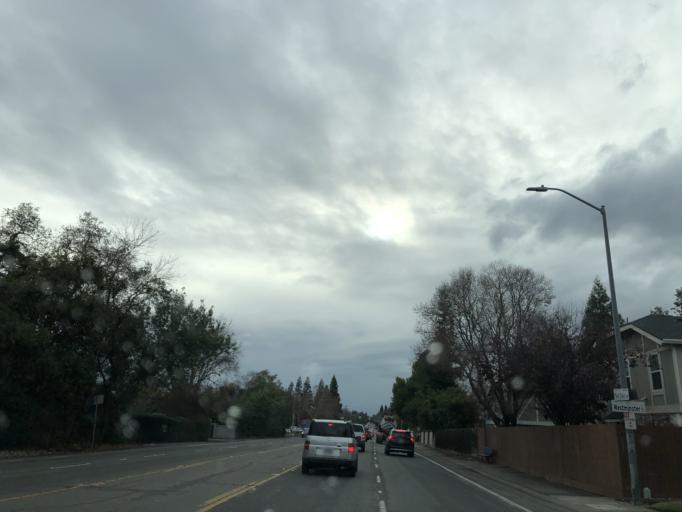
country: US
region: California
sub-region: Sacramento County
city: Carmichael
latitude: 38.5986
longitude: -121.3431
